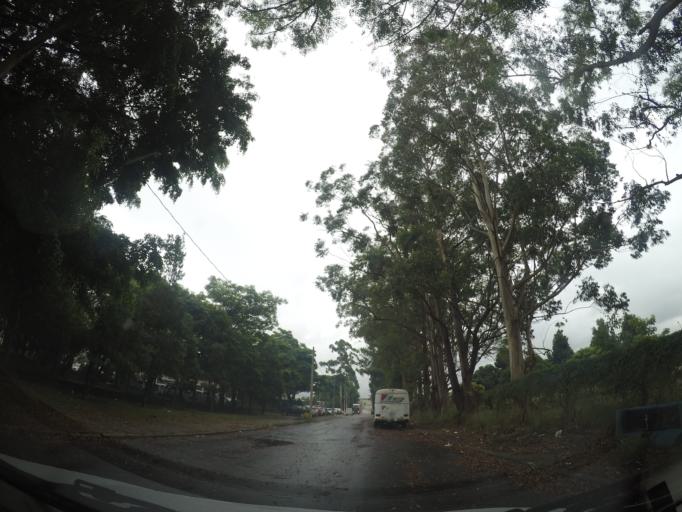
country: BR
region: Sao Paulo
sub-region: Guarulhos
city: Guarulhos
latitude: -23.4809
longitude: -46.4571
